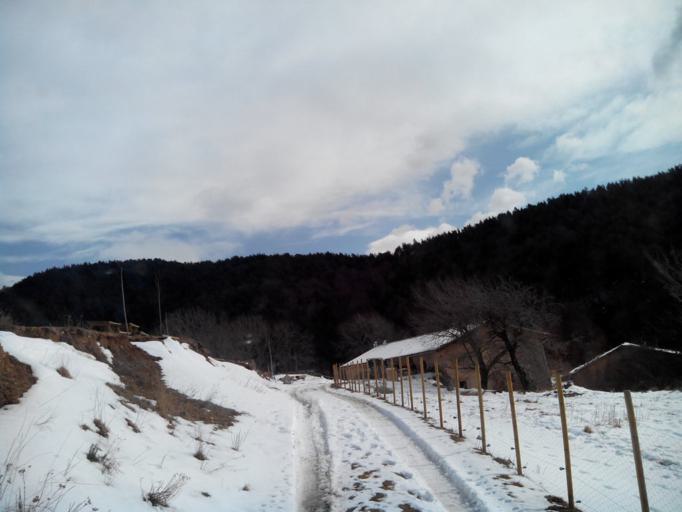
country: ES
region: Catalonia
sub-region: Provincia de Barcelona
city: Sant Julia de Cerdanyola
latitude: 42.1965
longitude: 1.9454
